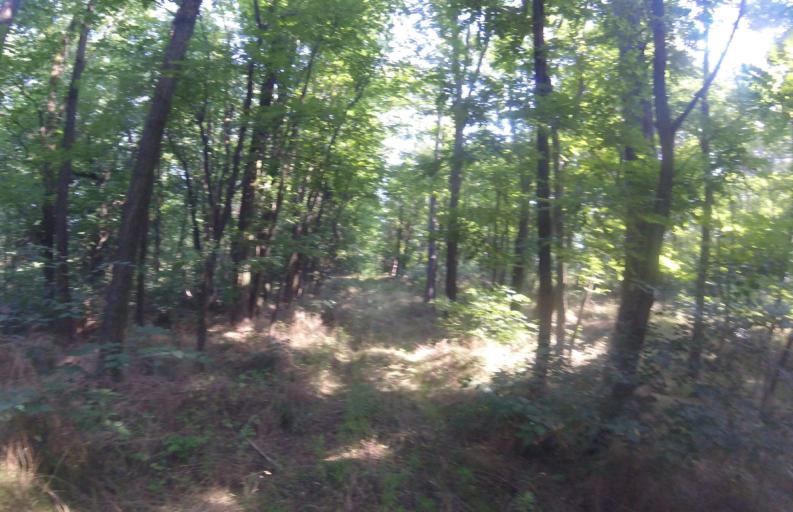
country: HU
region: Pest
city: Fot
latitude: 47.6375
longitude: 19.2161
